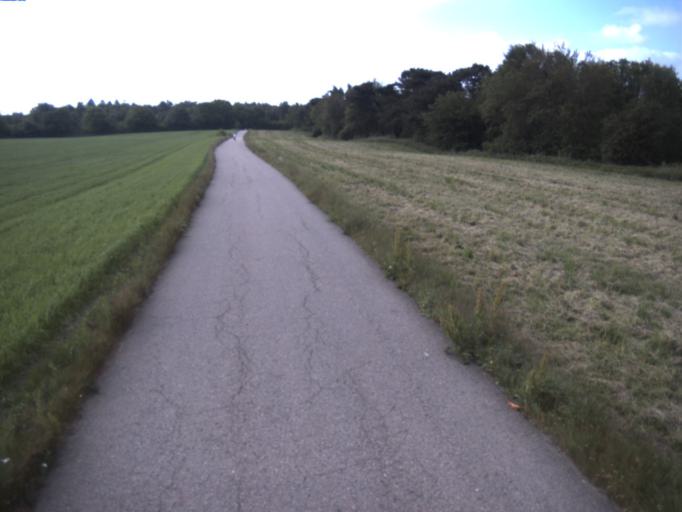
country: SE
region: Skane
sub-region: Helsingborg
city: Helsingborg
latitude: 56.0763
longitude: 12.6678
